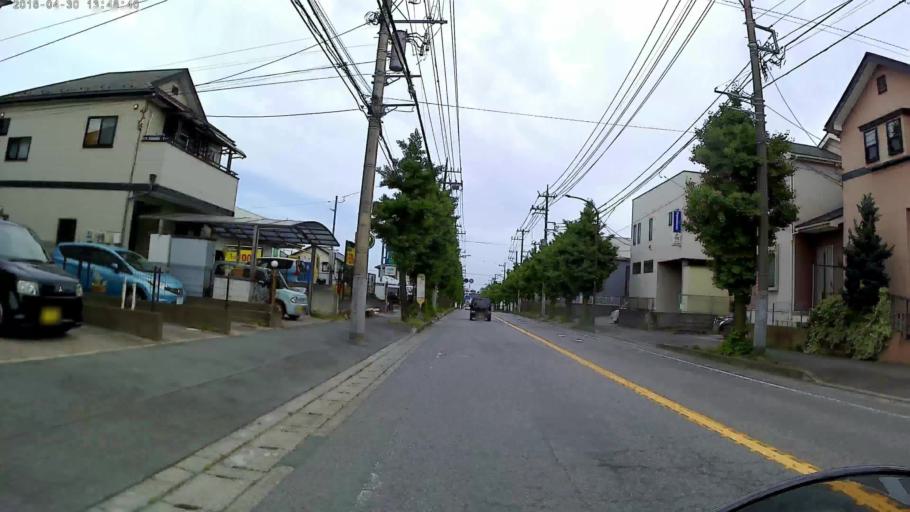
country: JP
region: Tokyo
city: Hachioji
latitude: 35.5932
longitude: 139.3643
